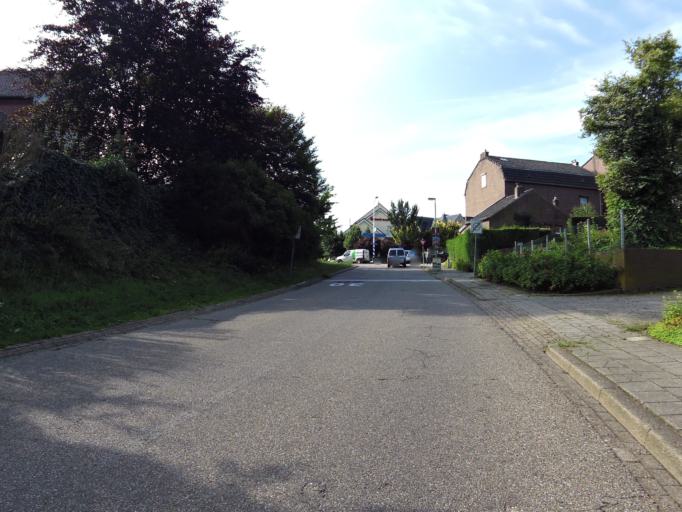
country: NL
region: Limburg
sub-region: Gemeente Voerendaal
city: Klimmen
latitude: 50.8783
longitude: 5.8861
